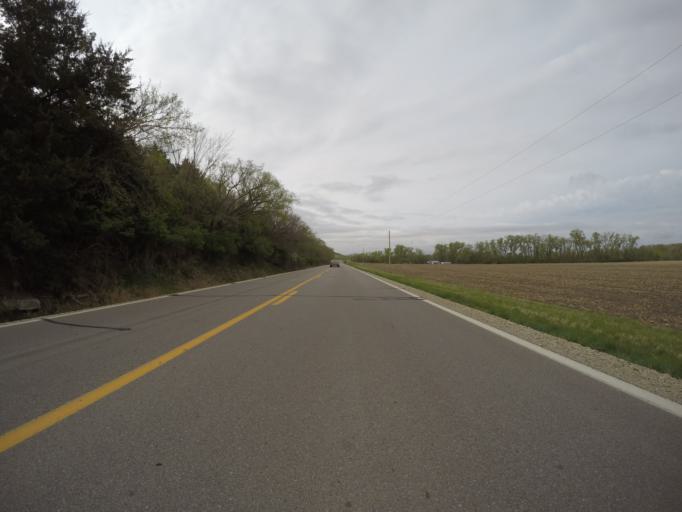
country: US
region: Kansas
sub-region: Riley County
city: Manhattan
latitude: 39.1516
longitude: -96.5578
